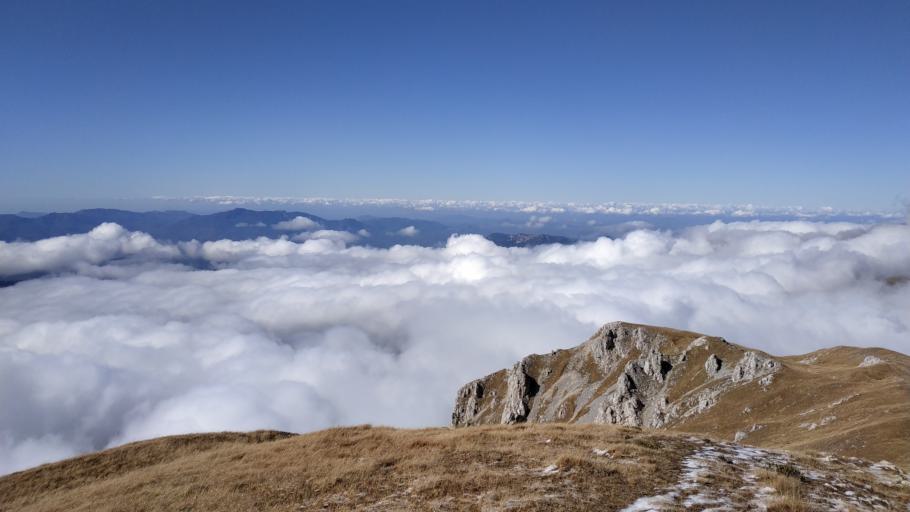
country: RU
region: Krasnodarskiy
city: Dagomys
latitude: 43.9991
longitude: 39.8789
